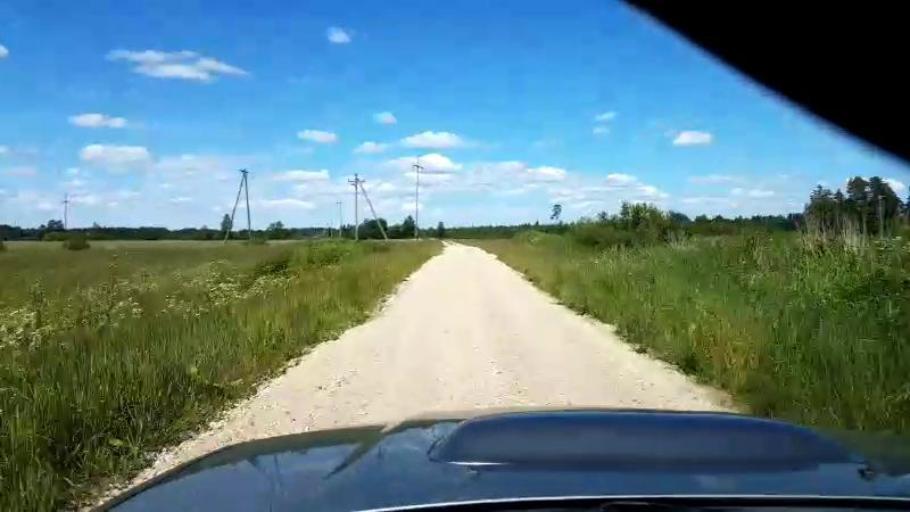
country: EE
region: Paernumaa
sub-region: Halinga vald
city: Parnu-Jaagupi
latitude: 58.5327
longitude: 24.5306
